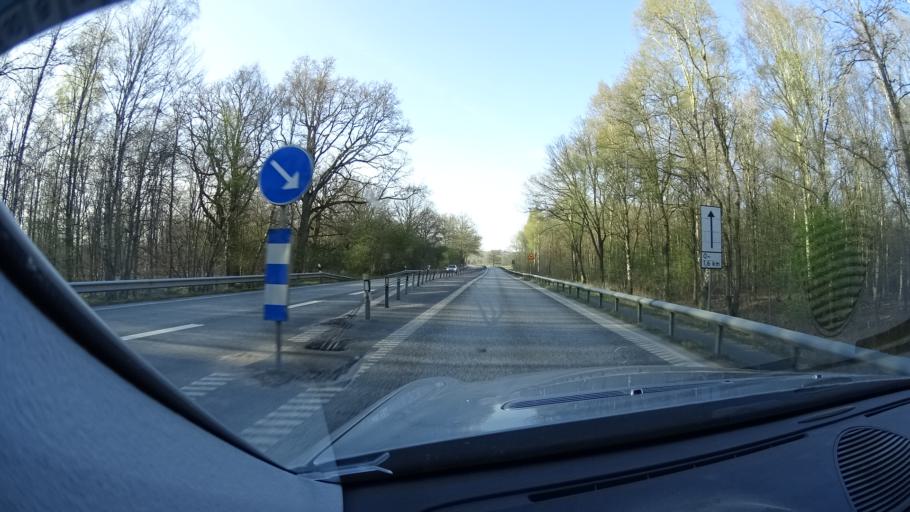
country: SE
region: Skane
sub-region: Hoors Kommun
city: Satofta
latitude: 55.8884
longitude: 13.5231
